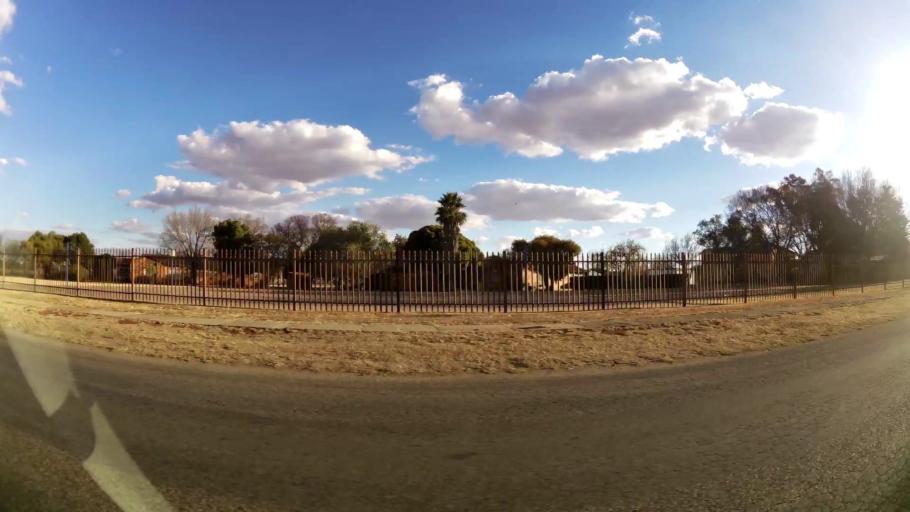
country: ZA
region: North-West
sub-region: Dr Kenneth Kaunda District Municipality
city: Potchefstroom
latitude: -26.7401
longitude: 27.0848
